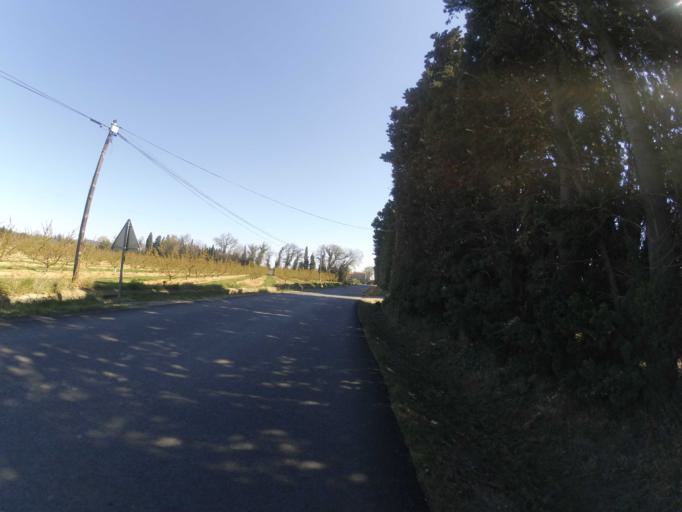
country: FR
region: Languedoc-Roussillon
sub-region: Departement des Pyrenees-Orientales
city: Ille-sur-Tet
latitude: 42.6722
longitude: 2.6557
